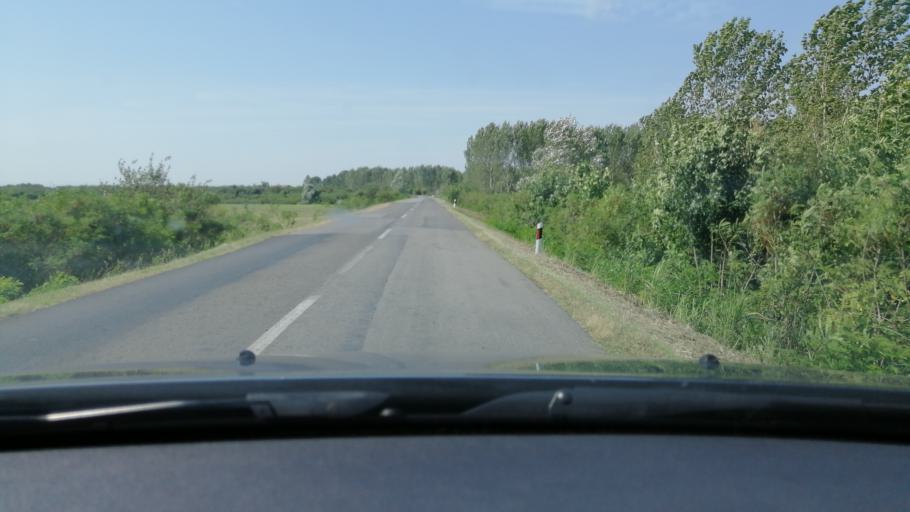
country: RS
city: Tomasevac
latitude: 45.2524
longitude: 20.6083
